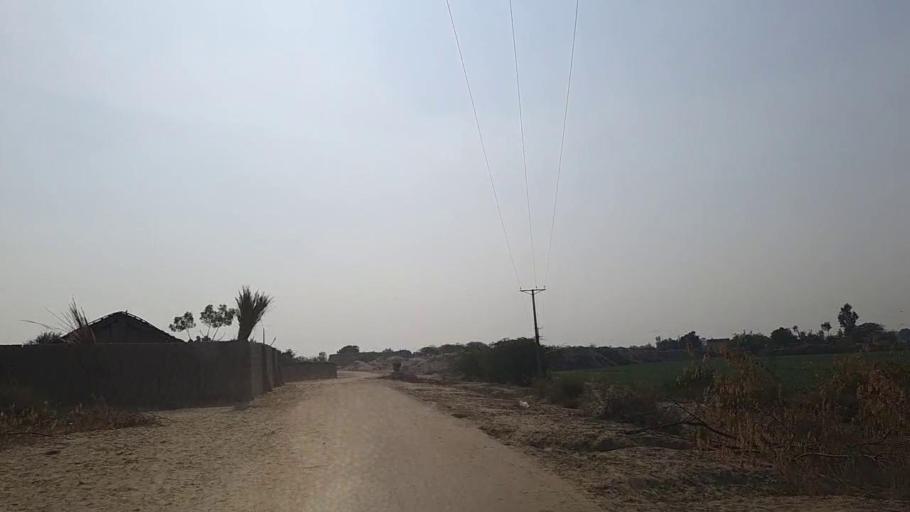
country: PK
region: Sindh
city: Daur
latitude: 26.4617
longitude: 68.4649
